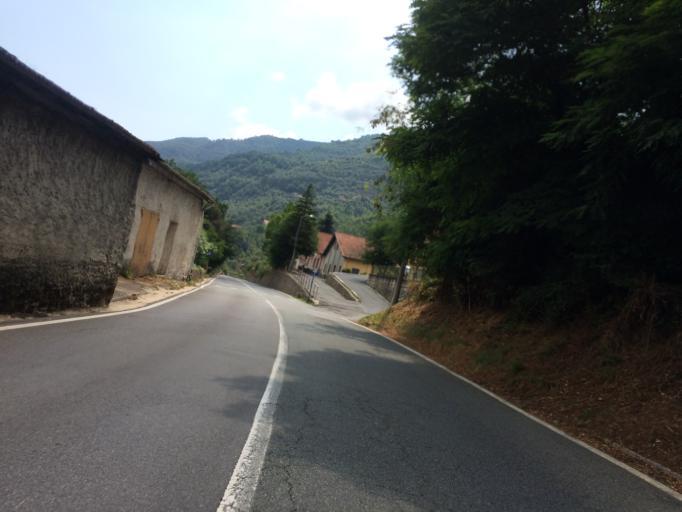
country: IT
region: Liguria
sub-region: Provincia di Imperia
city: Pigna
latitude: 43.9292
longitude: 7.6502
